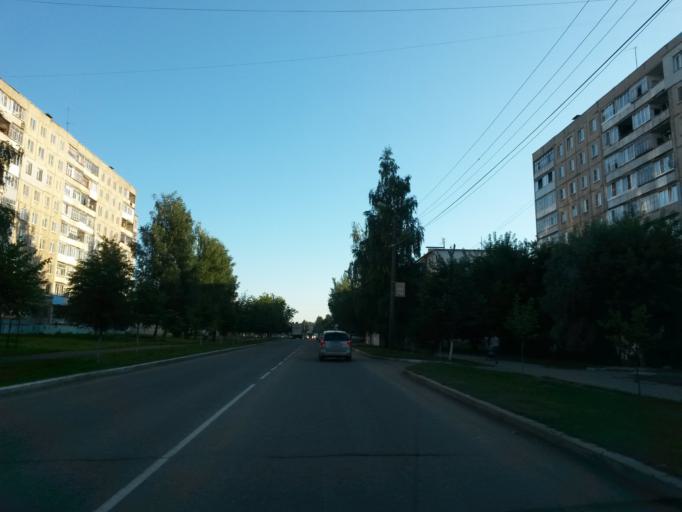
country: RU
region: Jaroslavl
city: Tutayev
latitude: 57.8683
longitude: 39.5182
